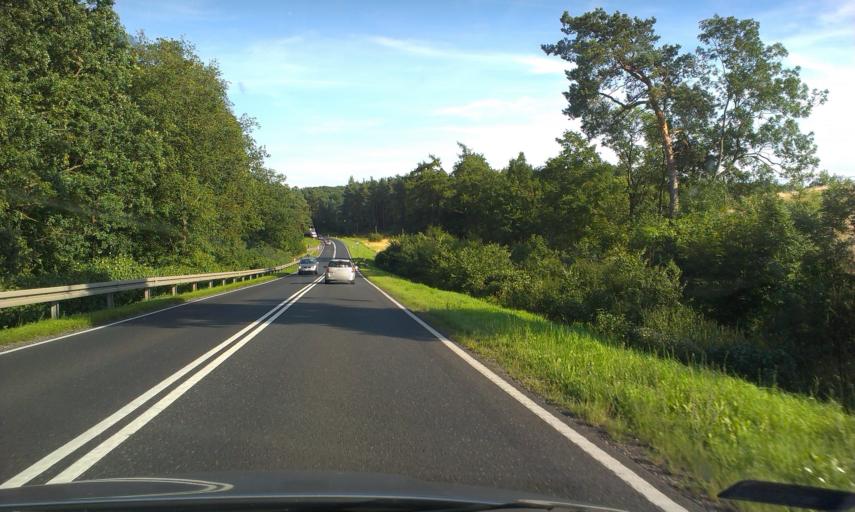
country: PL
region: Kujawsko-Pomorskie
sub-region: Powiat bydgoski
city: Sicienko
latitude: 53.1634
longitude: 17.7898
